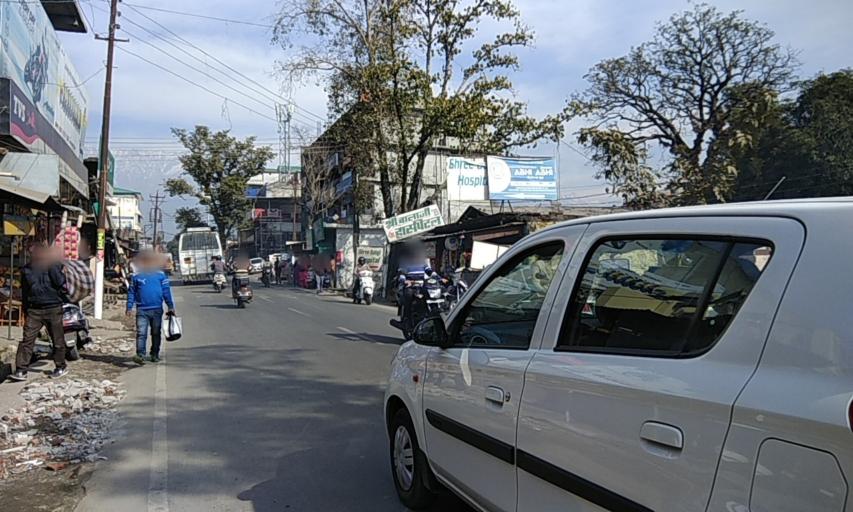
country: IN
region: Himachal Pradesh
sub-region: Kangra
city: Kangra
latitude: 32.1132
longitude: 76.2805
